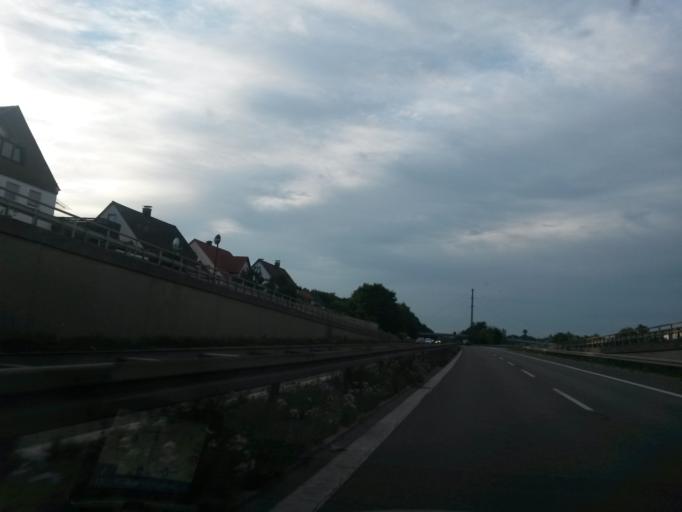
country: DE
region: Bavaria
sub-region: Regierungsbezirk Mittelfranken
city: Grossreuth bei Schweinau
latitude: 49.4226
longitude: 11.0389
